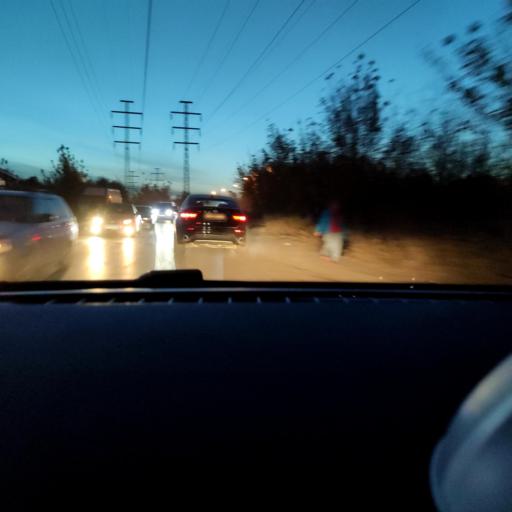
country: RU
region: Samara
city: Petra-Dubrava
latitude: 53.2950
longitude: 50.3022
